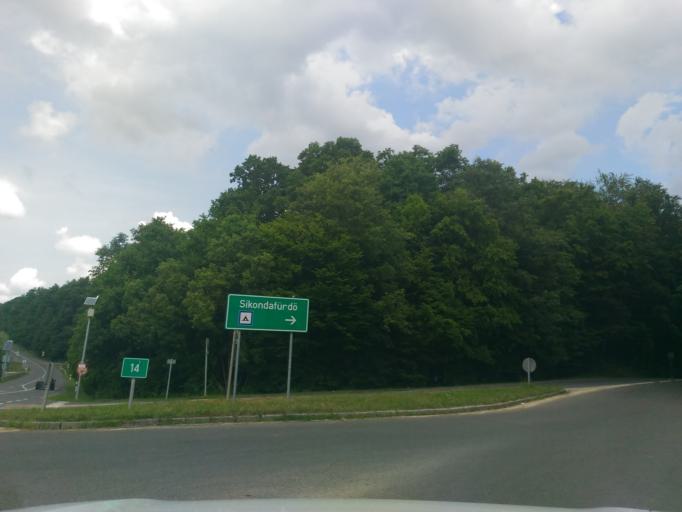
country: HU
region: Baranya
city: Komlo
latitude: 46.1800
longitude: 18.2094
